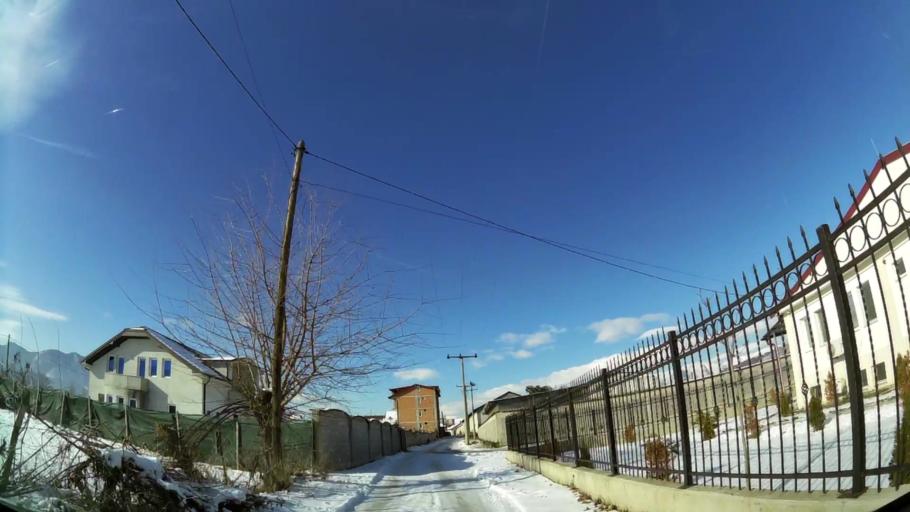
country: MK
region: Saraj
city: Saraj
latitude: 42.0011
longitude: 21.3355
